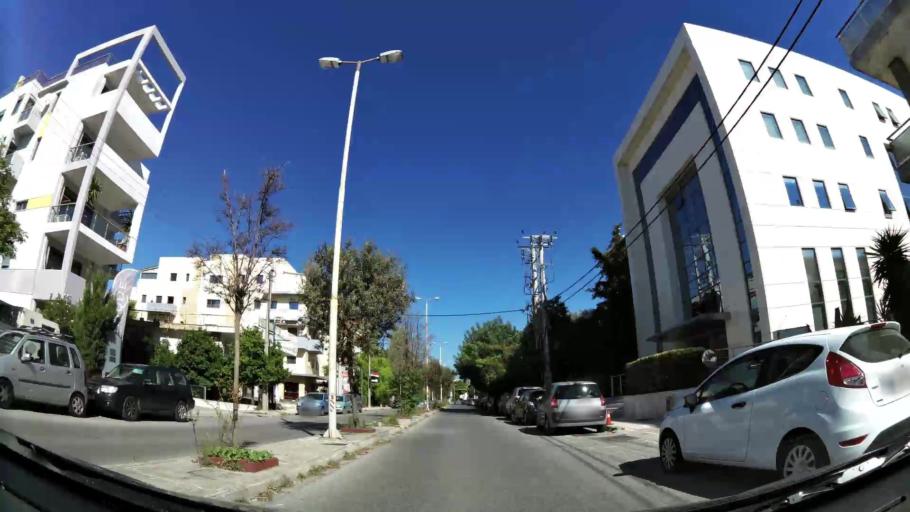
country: GR
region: Attica
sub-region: Nomarchia Athinas
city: Khalandrion
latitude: 38.0315
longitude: 23.8031
